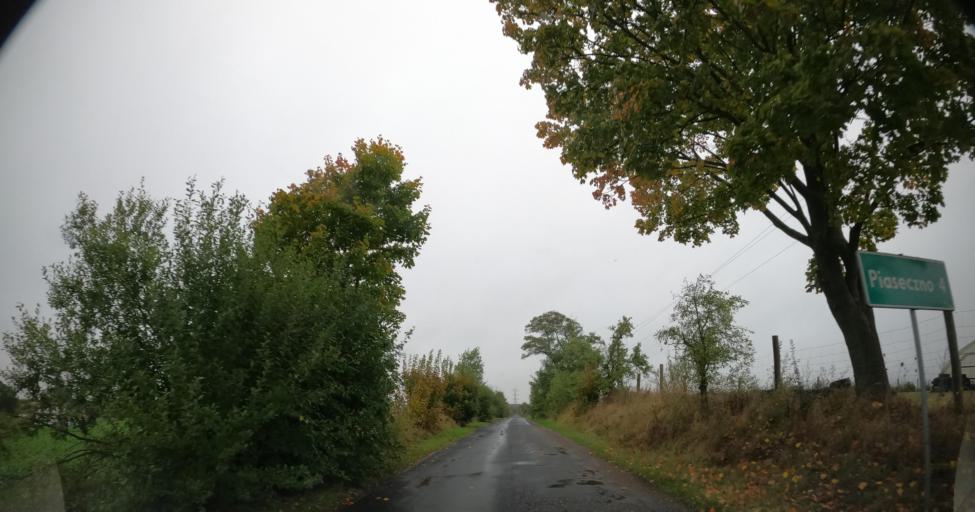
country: PL
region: West Pomeranian Voivodeship
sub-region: Powiat pyrzycki
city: Kozielice
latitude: 53.0476
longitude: 14.7613
